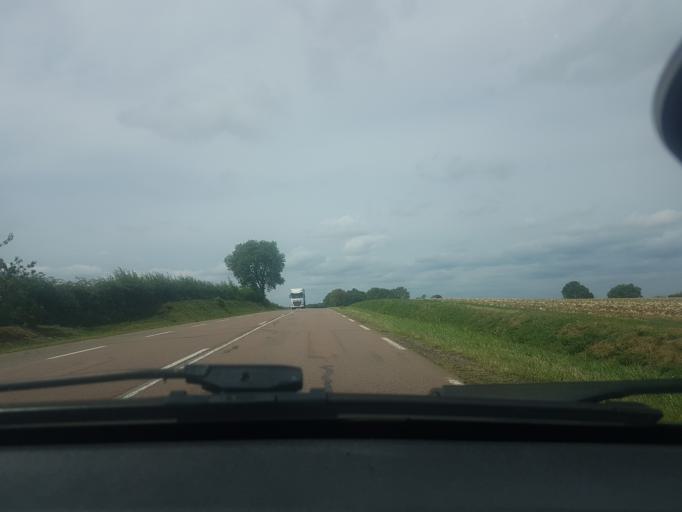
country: FR
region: Bourgogne
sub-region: Departement de la Cote-d'Or
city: Nolay
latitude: 47.0335
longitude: 4.6355
